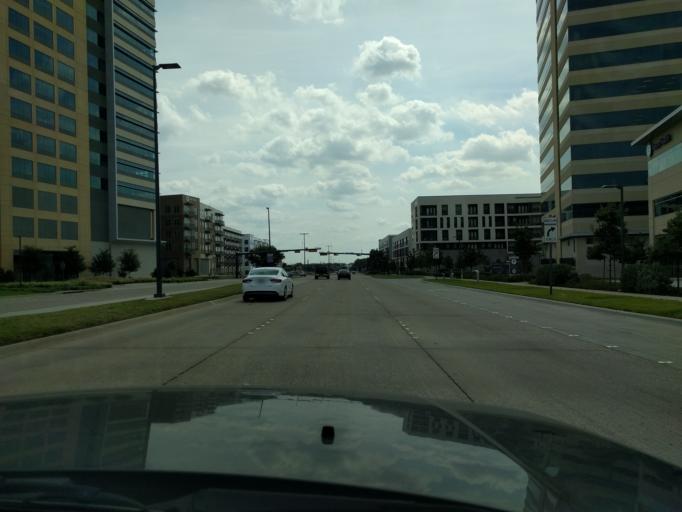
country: US
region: Texas
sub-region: Collin County
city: Plano
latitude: 33.0025
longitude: -96.6995
